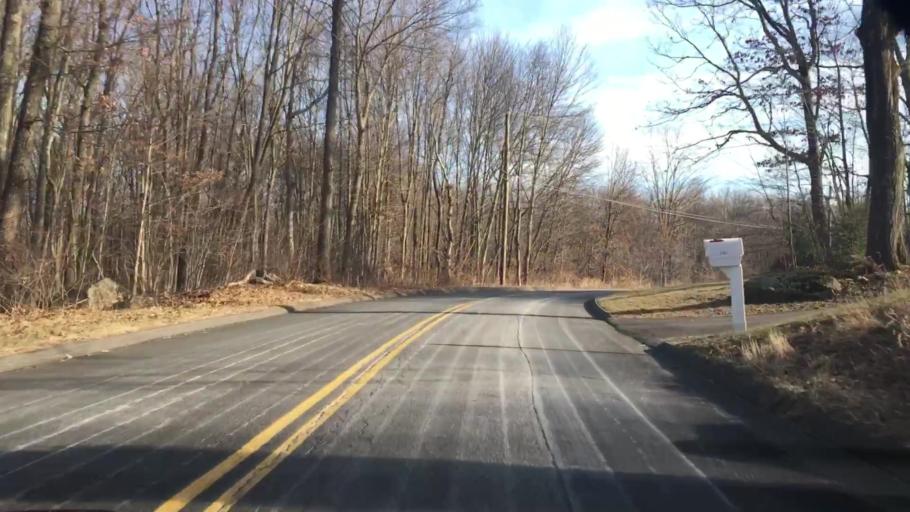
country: US
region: Connecticut
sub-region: New Haven County
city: Prospect
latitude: 41.5324
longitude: -72.9635
